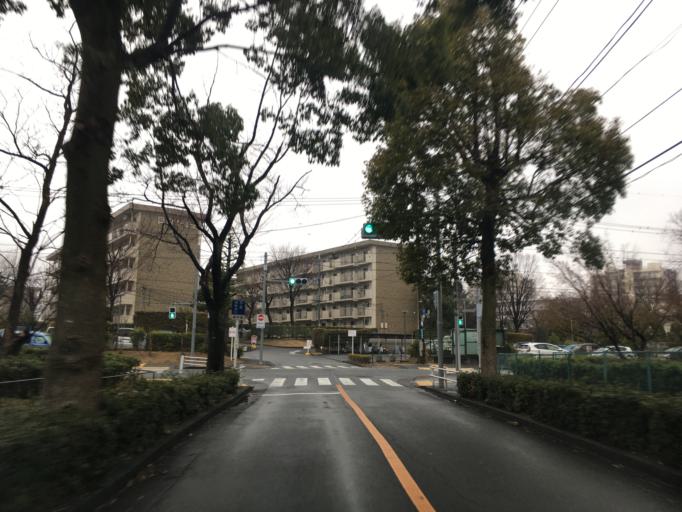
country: JP
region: Tokyo
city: Hino
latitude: 35.6136
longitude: 139.4406
